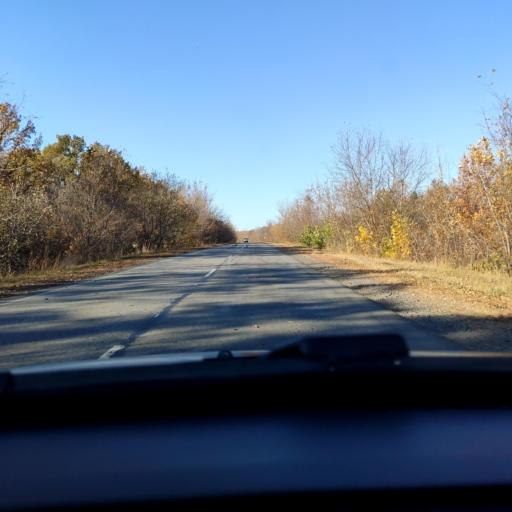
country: RU
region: Voronezj
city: Latnaya
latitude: 51.7990
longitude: 38.8720
